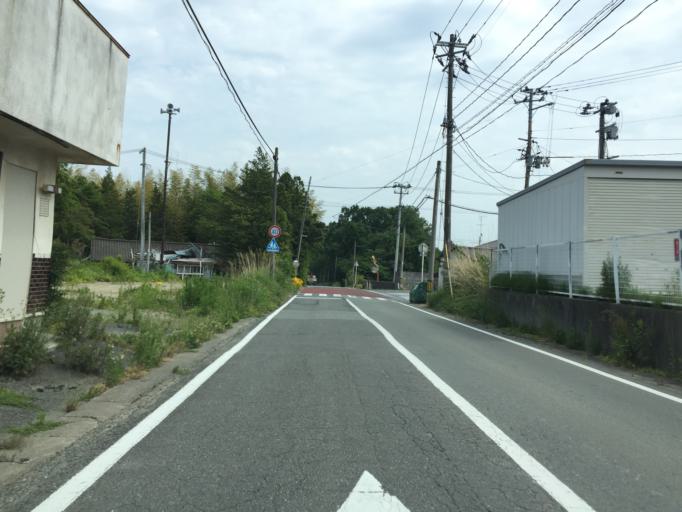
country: JP
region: Fukushima
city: Namie
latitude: 37.2942
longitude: 140.9999
